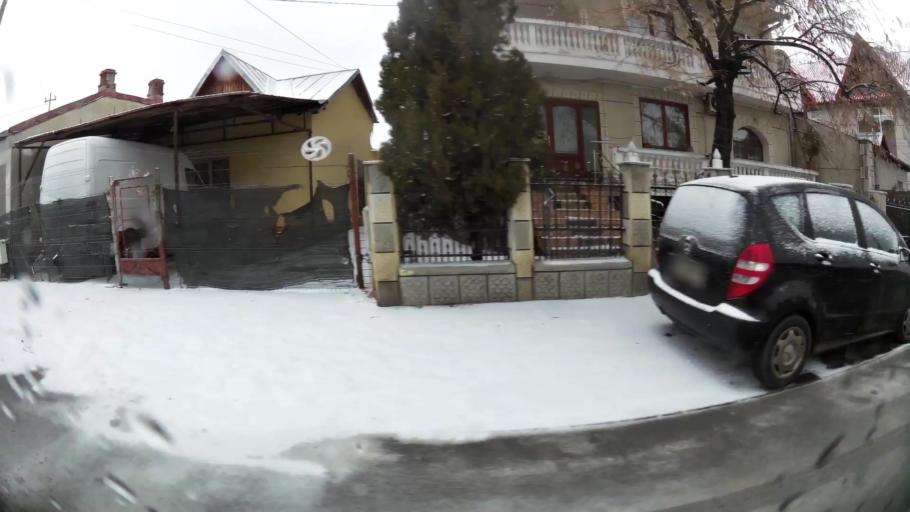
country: RO
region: Prahova
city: Ploiesti
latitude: 44.9243
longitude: 26.0149
